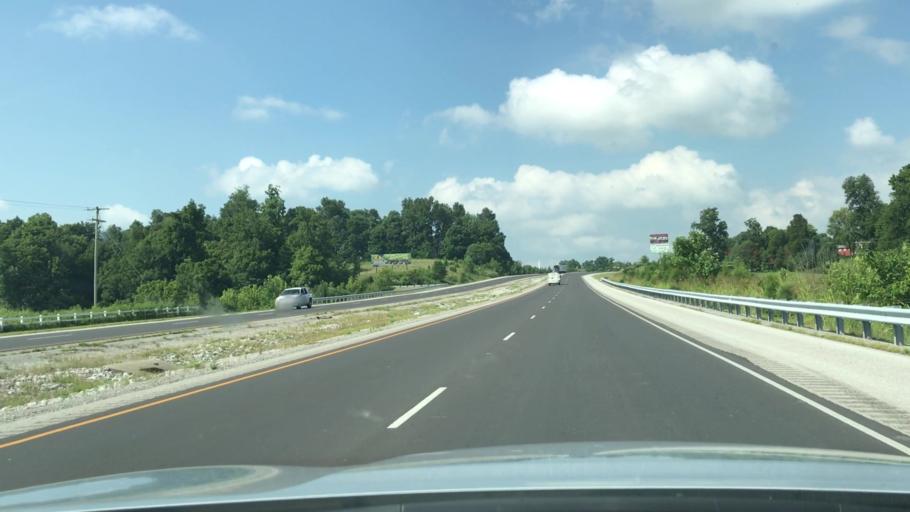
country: US
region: Kentucky
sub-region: Barren County
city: Glasgow
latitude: 37.0188
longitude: -85.9439
